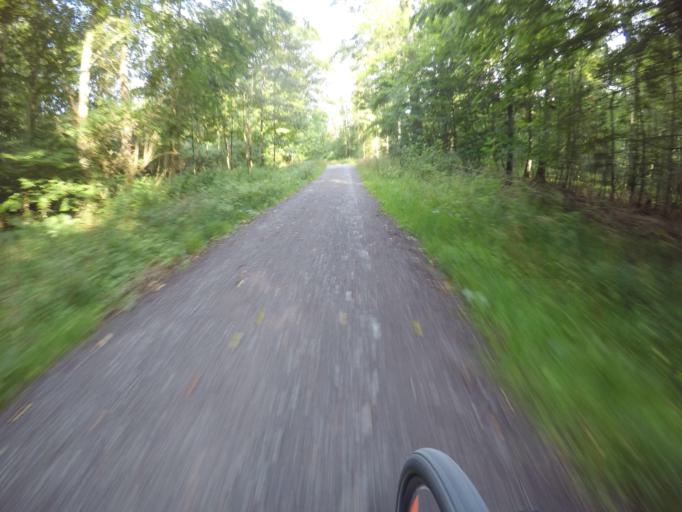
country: DE
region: Baden-Wuerttemberg
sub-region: Regierungsbezirk Stuttgart
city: Rutesheim
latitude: 48.8354
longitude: 8.9566
